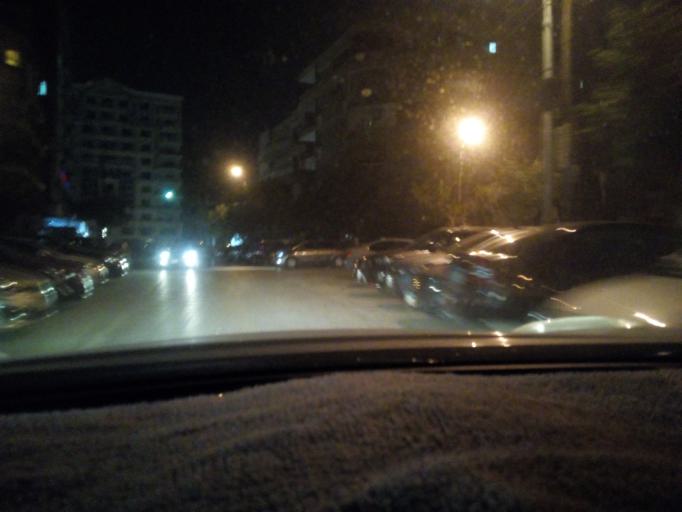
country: EG
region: Muhafazat al Qahirah
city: Cairo
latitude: 30.0868
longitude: 31.3450
